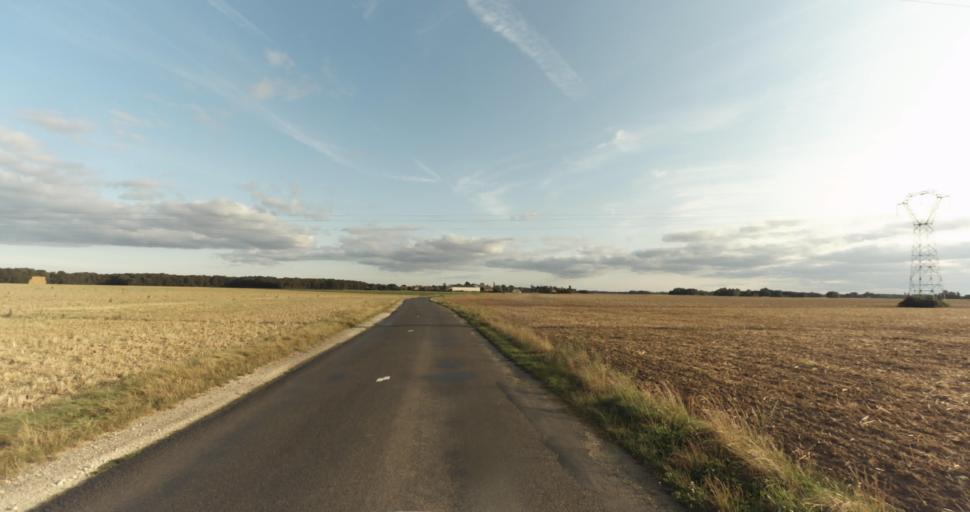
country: FR
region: Haute-Normandie
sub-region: Departement de l'Eure
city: Marcilly-sur-Eure
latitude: 48.8560
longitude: 1.2743
